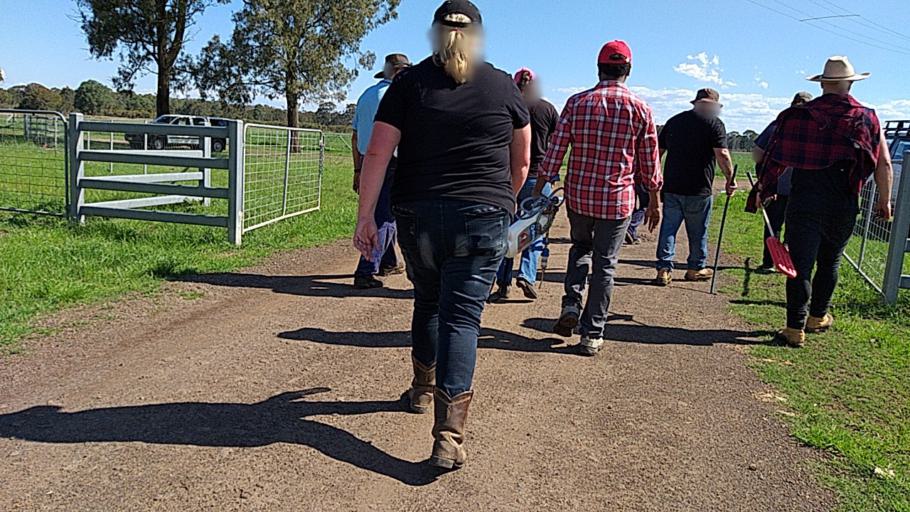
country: AU
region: New South Wales
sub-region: Hawkesbury
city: Richmond
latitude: -33.6186
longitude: 150.7578
